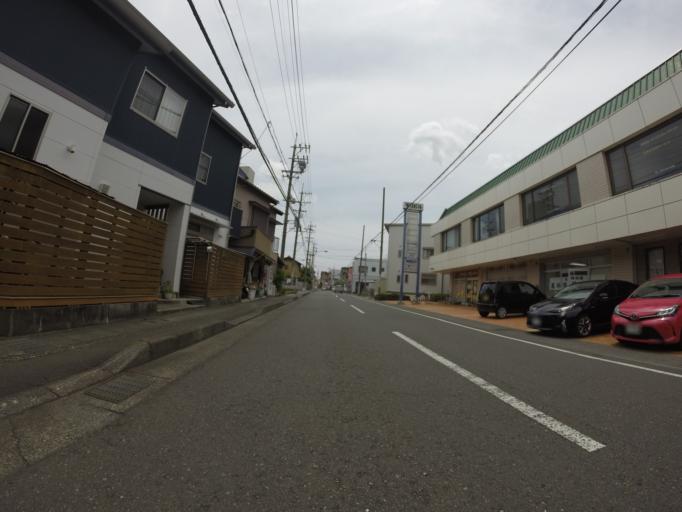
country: JP
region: Shizuoka
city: Shizuoka-shi
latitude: 35.0013
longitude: 138.4117
